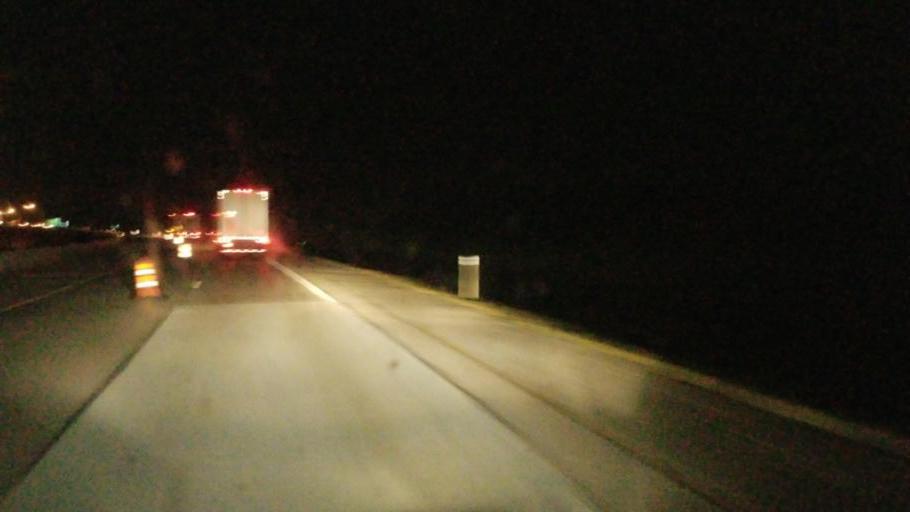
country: US
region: Indiana
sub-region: Allen County
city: New Haven
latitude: 41.1264
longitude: -84.9965
